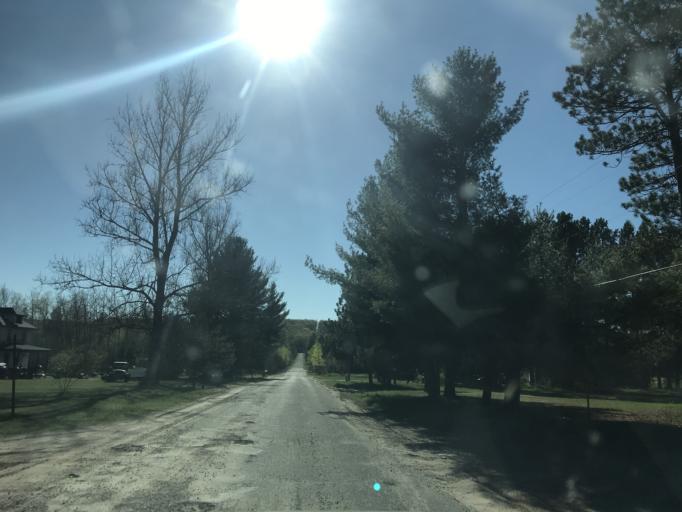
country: US
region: Michigan
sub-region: Crawford County
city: Grayling
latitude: 44.7713
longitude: -84.7608
